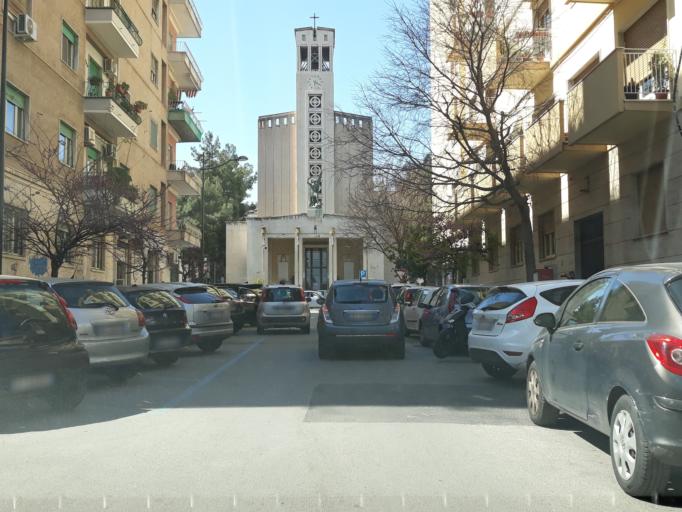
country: IT
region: Sicily
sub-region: Palermo
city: Palermo
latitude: 38.1351
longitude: 13.3434
